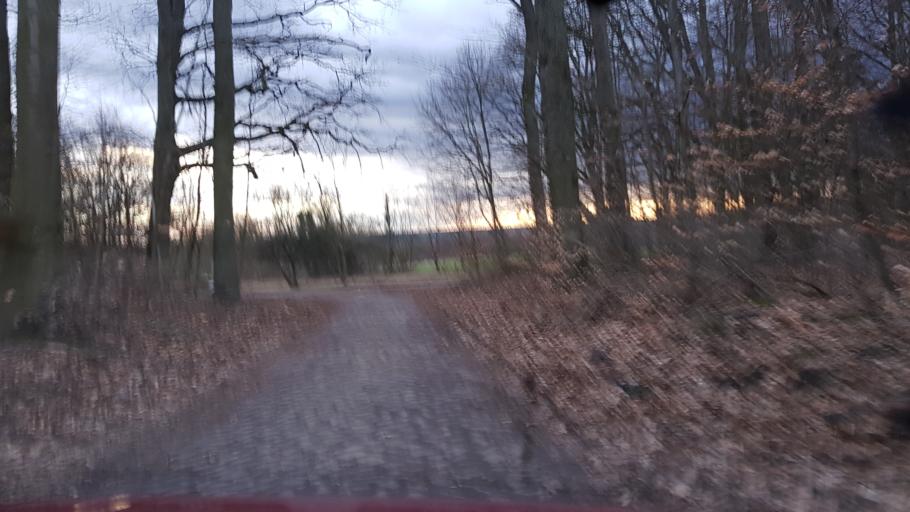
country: PL
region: West Pomeranian Voivodeship
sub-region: Powiat gryfinski
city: Stare Czarnowo
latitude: 53.2974
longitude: 14.7253
